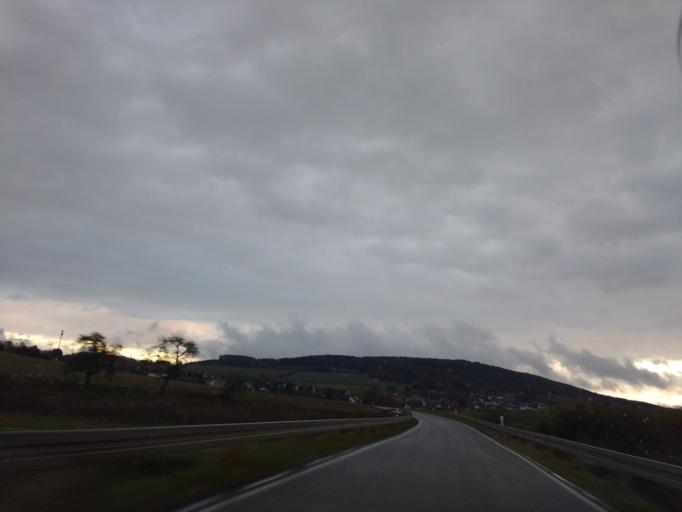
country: DE
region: Hesse
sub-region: Regierungsbezirk Kassel
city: Martinhagen
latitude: 51.2890
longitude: 9.3077
